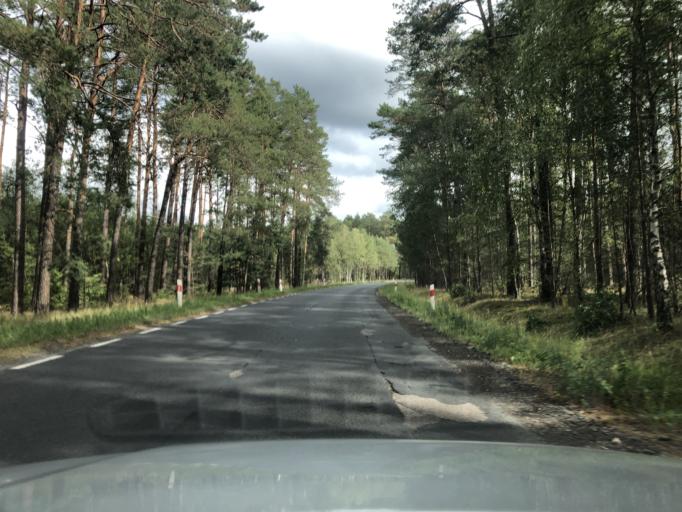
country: PL
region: Greater Poland Voivodeship
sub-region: Powiat czarnkowsko-trzcianecki
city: Krzyz Wielkopolski
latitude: 52.8569
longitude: 15.9278
